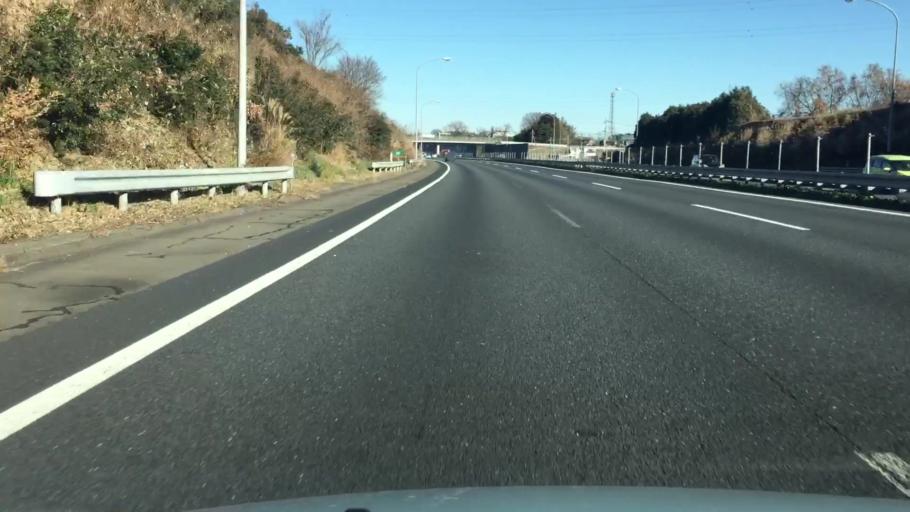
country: JP
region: Saitama
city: Sakado
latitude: 35.9963
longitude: 139.3872
